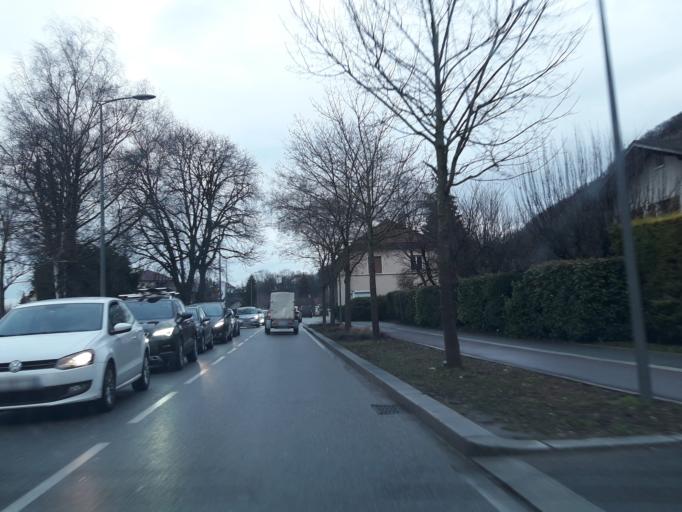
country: FR
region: Rhone-Alpes
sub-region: Departement de la Haute-Savoie
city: Etrembieres
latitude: 46.1756
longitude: 6.2220
